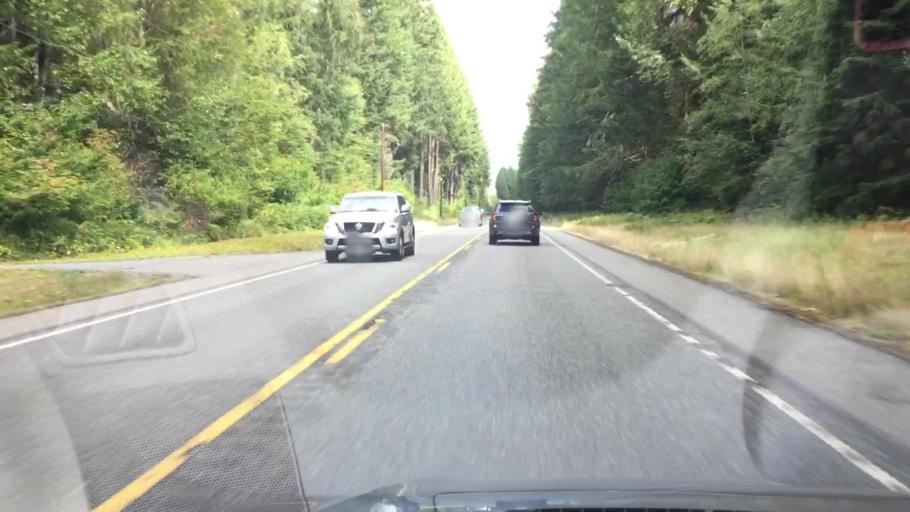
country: US
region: Washington
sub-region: Pierce County
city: Eatonville
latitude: 46.7540
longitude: -122.1052
